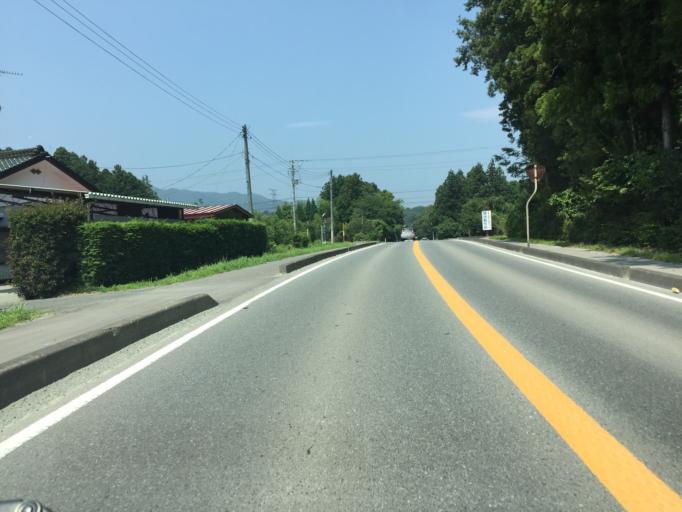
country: JP
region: Miyagi
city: Marumori
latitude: 37.8441
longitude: 140.8898
